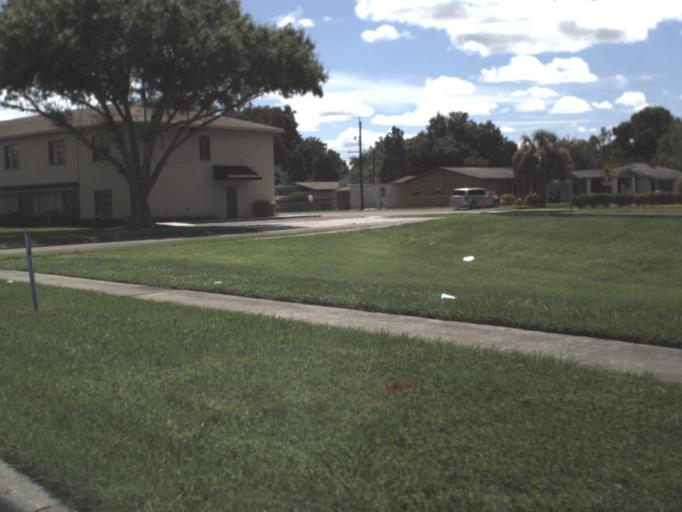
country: US
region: Florida
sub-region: Polk County
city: Lakeland
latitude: 28.0521
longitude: -81.9295
